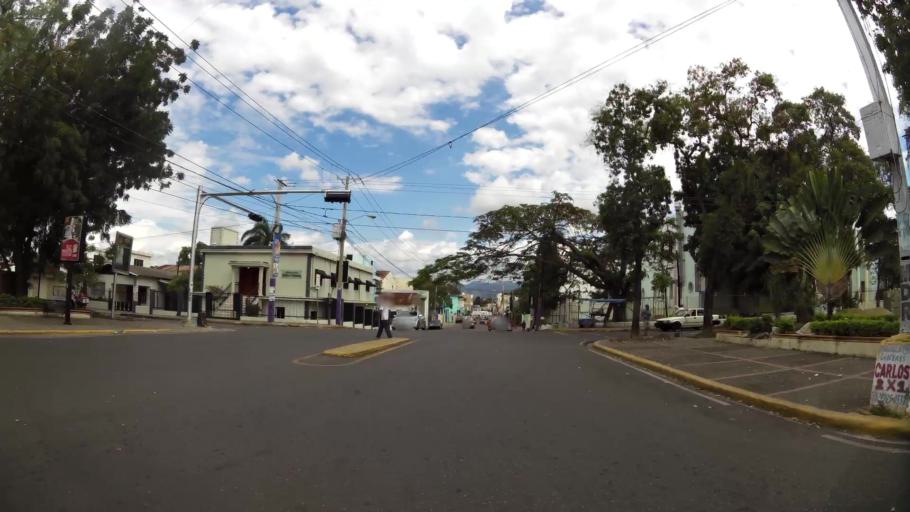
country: DO
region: Santiago
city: Santiago de los Caballeros
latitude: 19.4561
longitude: -70.7098
